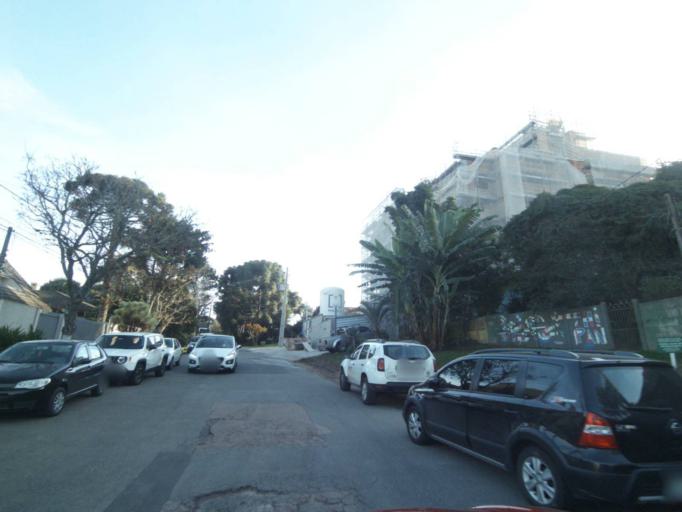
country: BR
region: Parana
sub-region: Curitiba
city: Curitiba
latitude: -25.4278
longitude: -49.2986
